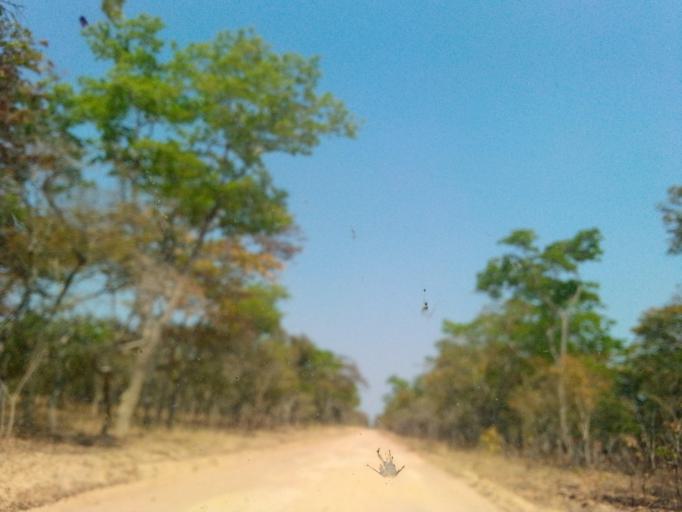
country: ZM
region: Northern
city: Mpika
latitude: -12.2419
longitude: 30.8528
